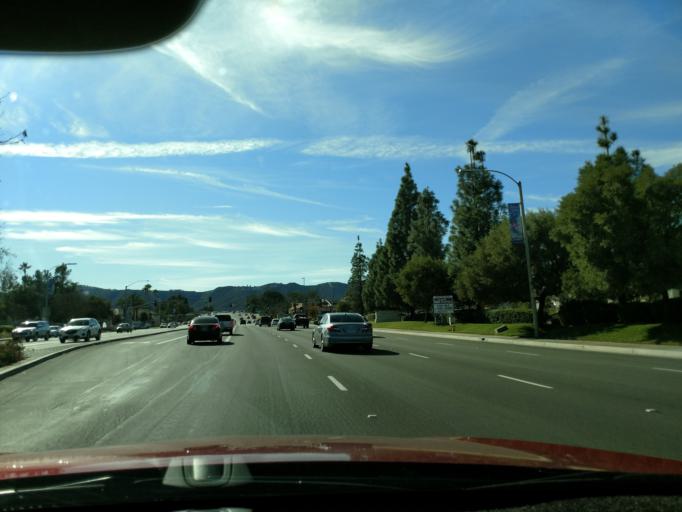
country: US
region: California
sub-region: Riverside County
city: Temecula
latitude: 33.5257
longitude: -117.1589
